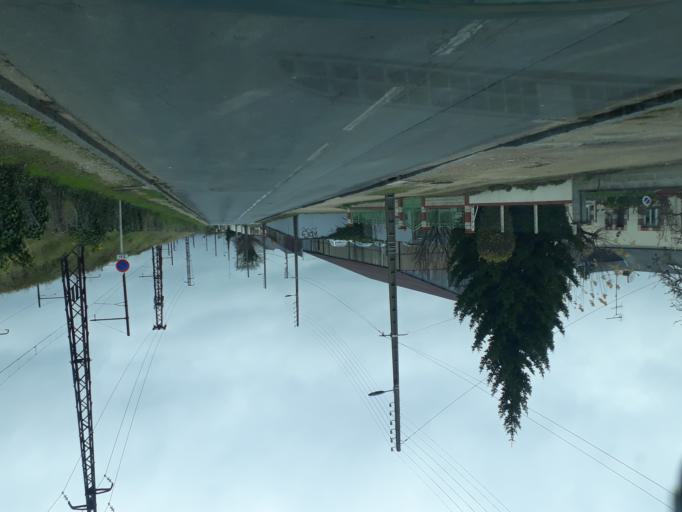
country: FR
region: Centre
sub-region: Departement du Loiret
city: Fleury-les-Aubrais
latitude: 47.9285
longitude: 1.9003
